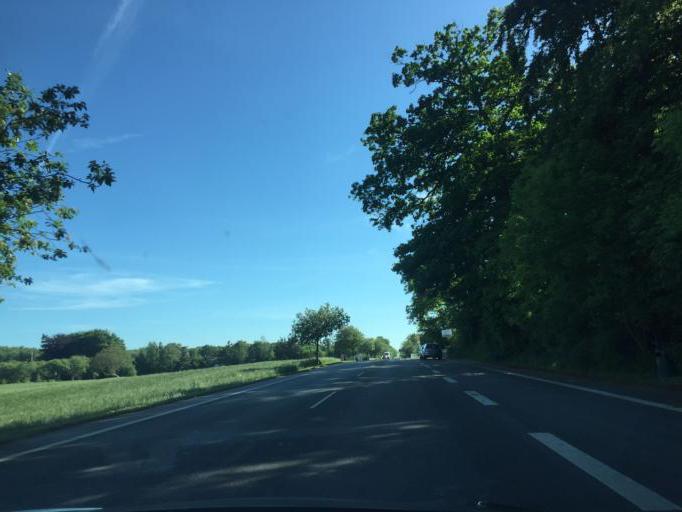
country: DK
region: Zealand
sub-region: Koge Kommune
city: Koge
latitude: 55.3975
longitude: 12.1203
